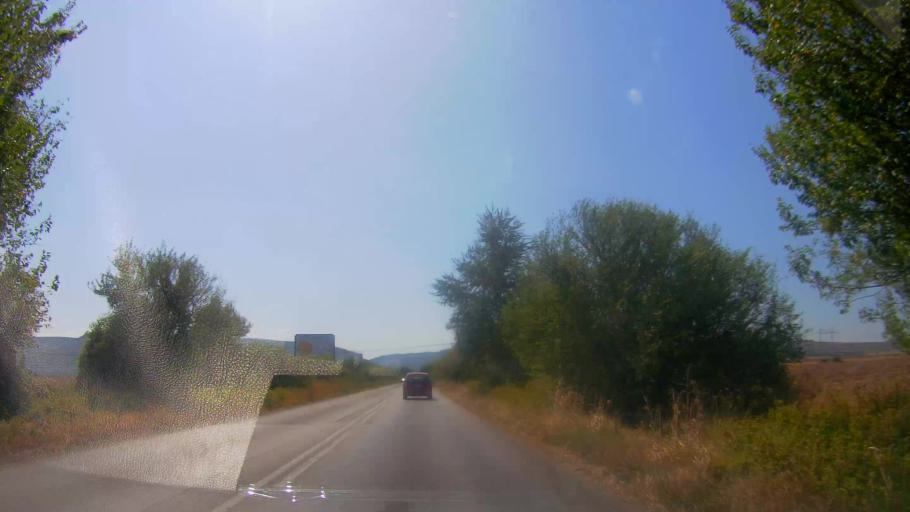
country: BG
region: Veliko Turnovo
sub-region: Obshtina Gorna Oryakhovitsa
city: Purvomaytsi
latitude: 43.1606
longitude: 25.6195
